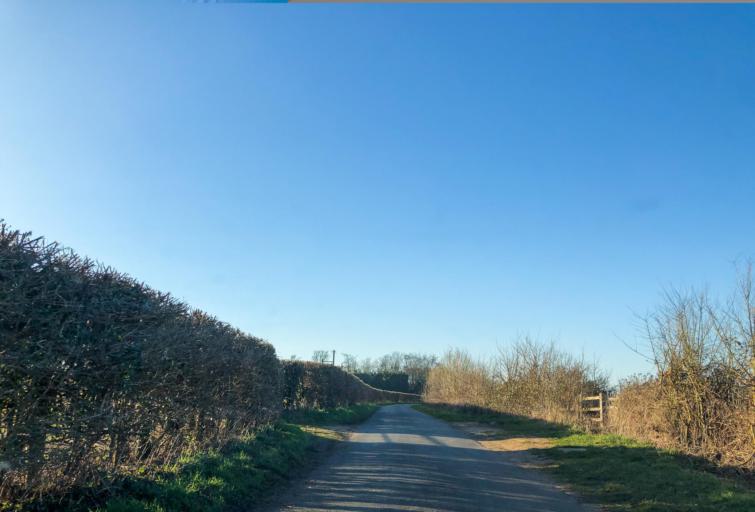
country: GB
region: England
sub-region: Warwickshire
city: Warwick
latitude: 52.2418
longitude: -1.5834
